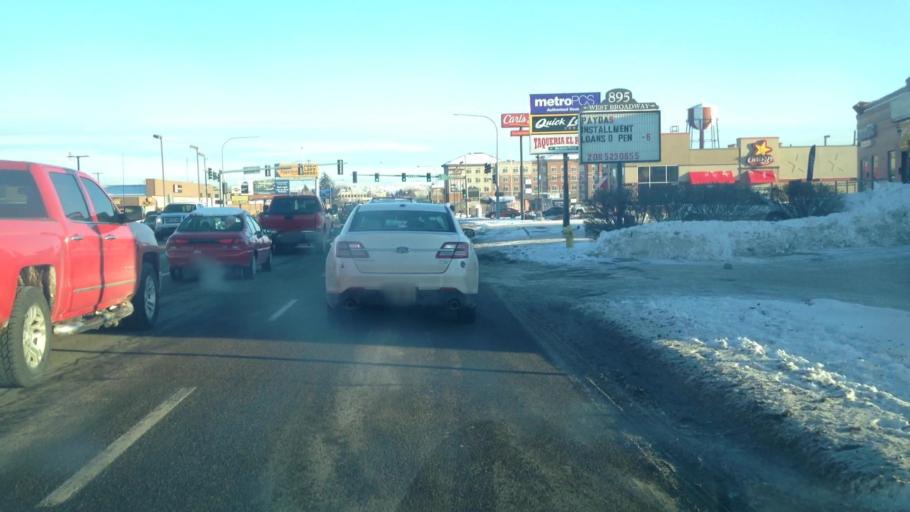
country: US
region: Idaho
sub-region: Bonneville County
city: Idaho Falls
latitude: 43.4949
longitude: -112.0494
